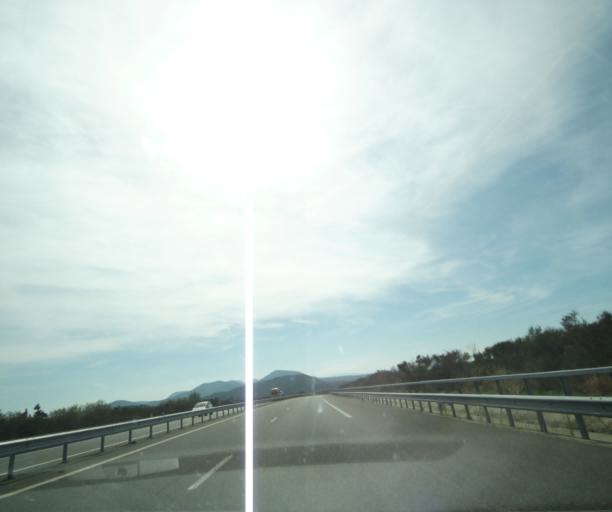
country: FR
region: Auvergne
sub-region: Departement du Puy-de-Dome
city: Manzat
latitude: 45.9199
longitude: 2.9593
